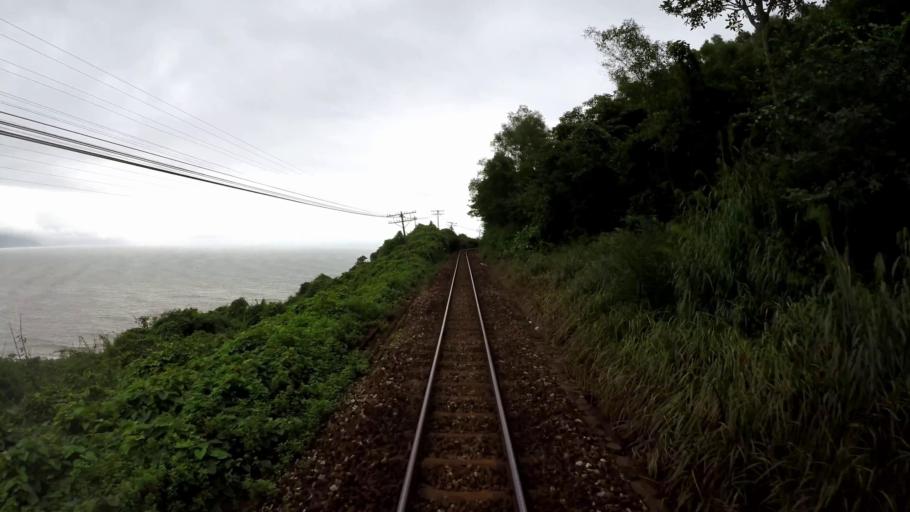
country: VN
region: Da Nang
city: Lien Chieu
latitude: 16.2097
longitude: 108.1227
